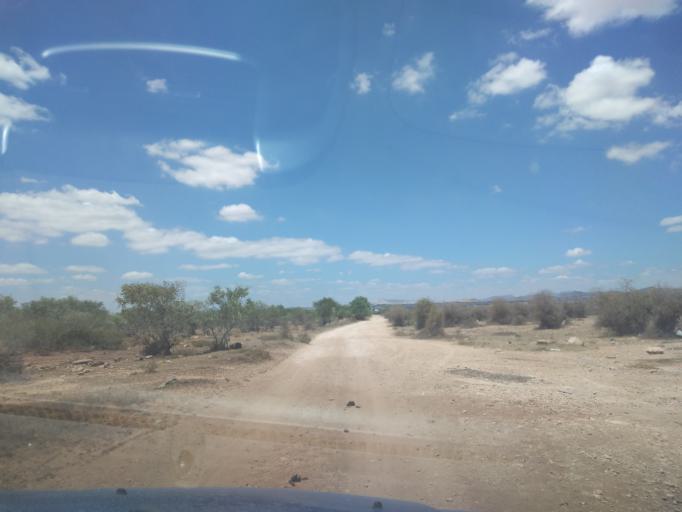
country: TN
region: Susah
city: Harqalah
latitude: 36.1662
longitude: 10.4425
